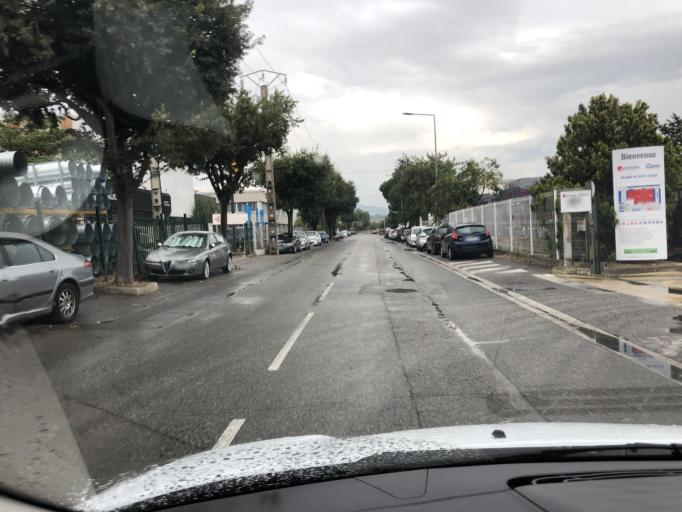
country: FR
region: Provence-Alpes-Cote d'Azur
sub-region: Departement des Bouches-du-Rhone
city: La Penne-sur-Huveaune
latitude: 43.2846
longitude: 5.5368
